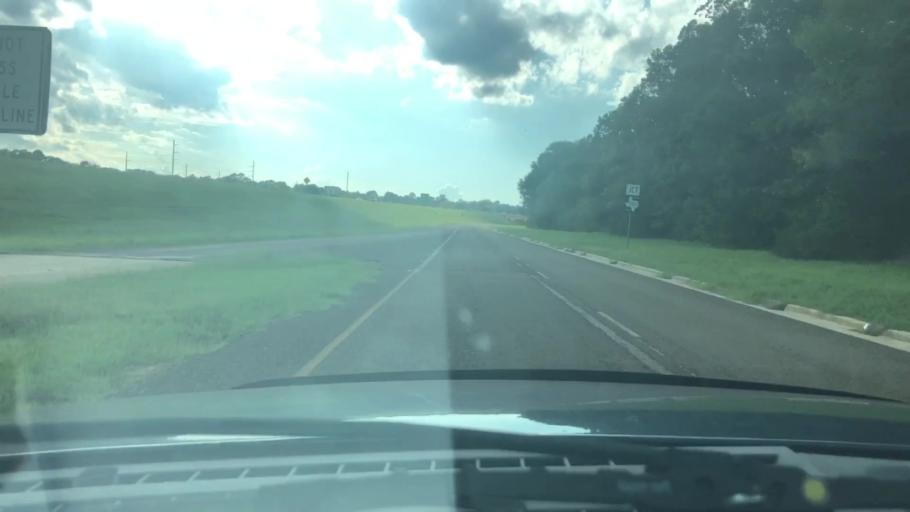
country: US
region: Texas
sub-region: Bowie County
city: Wake Village
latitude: 33.3865
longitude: -94.0862
